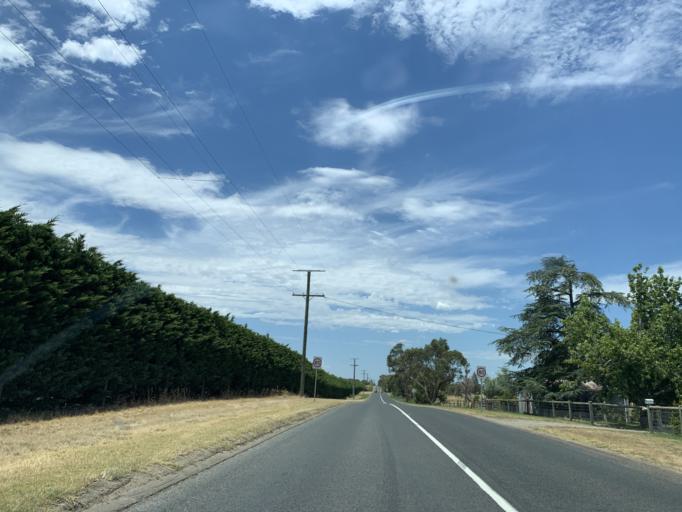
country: AU
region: Victoria
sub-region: Mornington Peninsula
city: Tyabb
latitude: -38.2386
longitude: 145.1967
